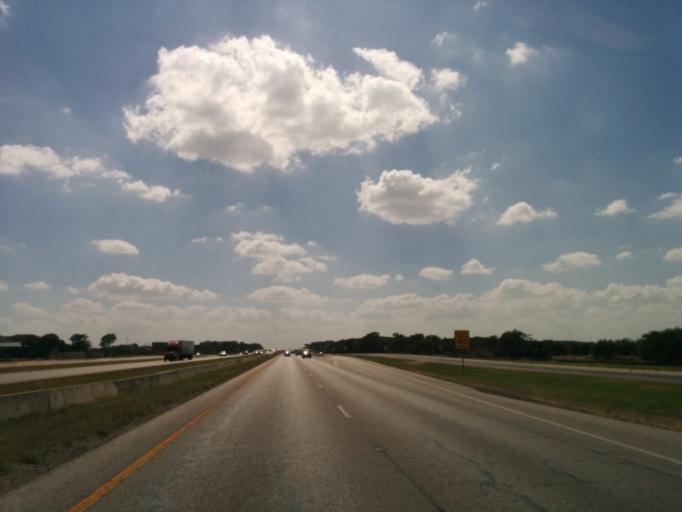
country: US
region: Texas
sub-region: Bexar County
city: Shavano Park
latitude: 29.6021
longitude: -98.5421
